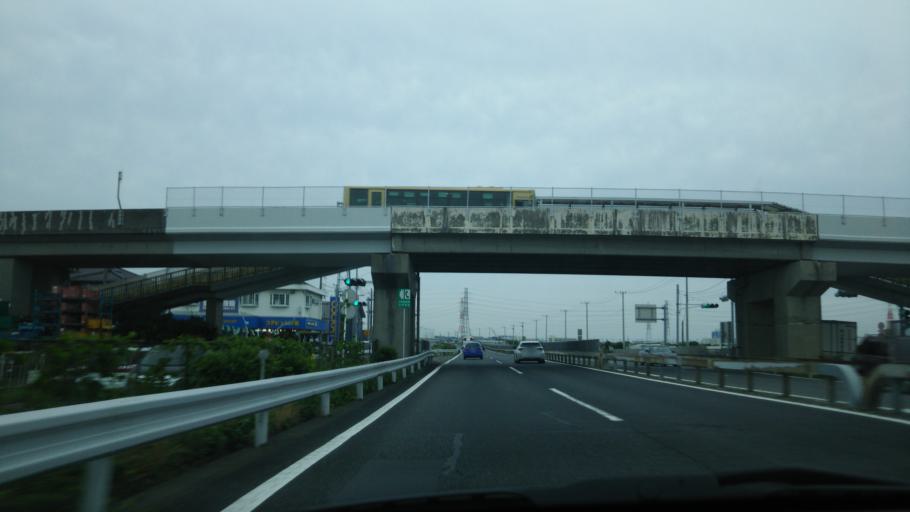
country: JP
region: Kanagawa
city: Isehara
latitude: 35.3907
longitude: 139.3331
